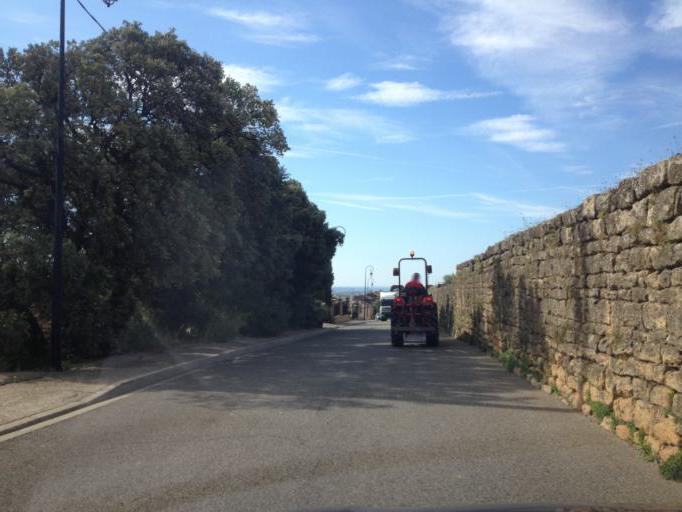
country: FR
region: Provence-Alpes-Cote d'Azur
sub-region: Departement du Vaucluse
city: Chateauneuf-du-Pape
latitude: 44.0604
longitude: 4.8293
